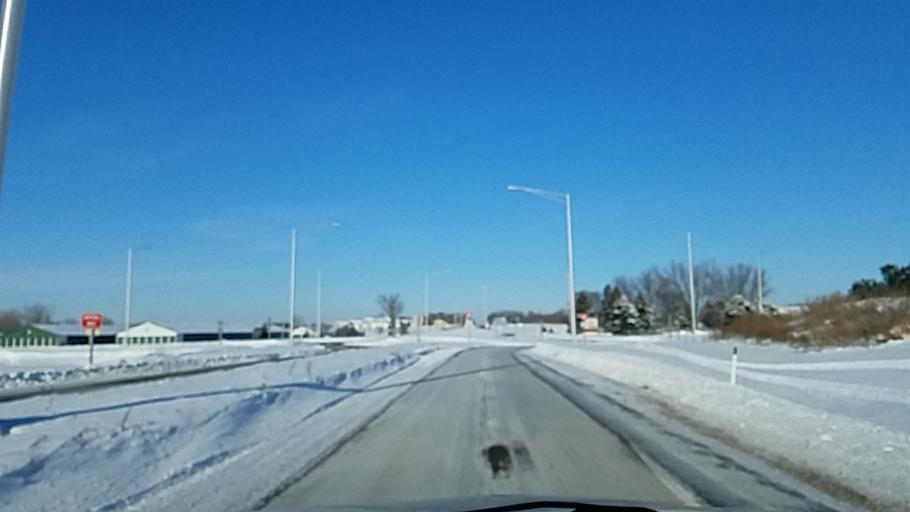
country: US
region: Wisconsin
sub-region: Saint Croix County
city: New Richmond
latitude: 45.0782
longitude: -92.5375
